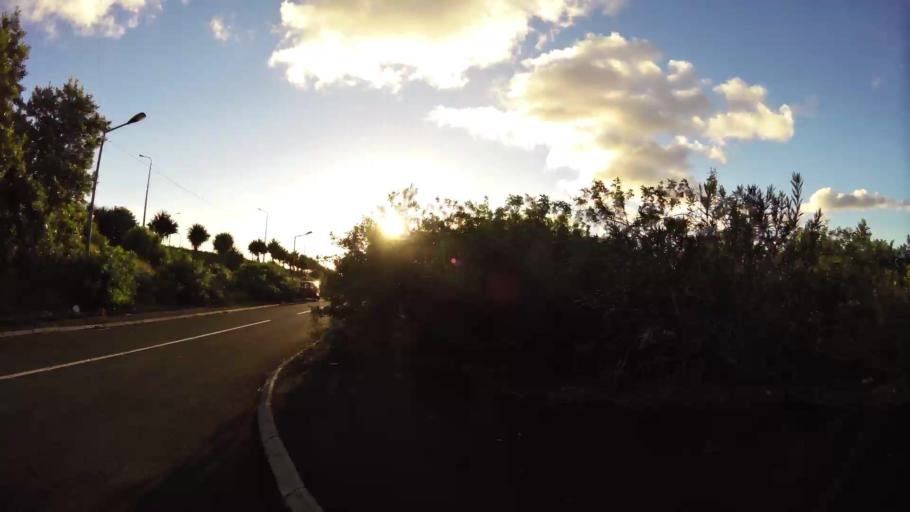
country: MU
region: Plaines Wilhems
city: Ebene
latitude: -20.2406
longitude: 57.4859
